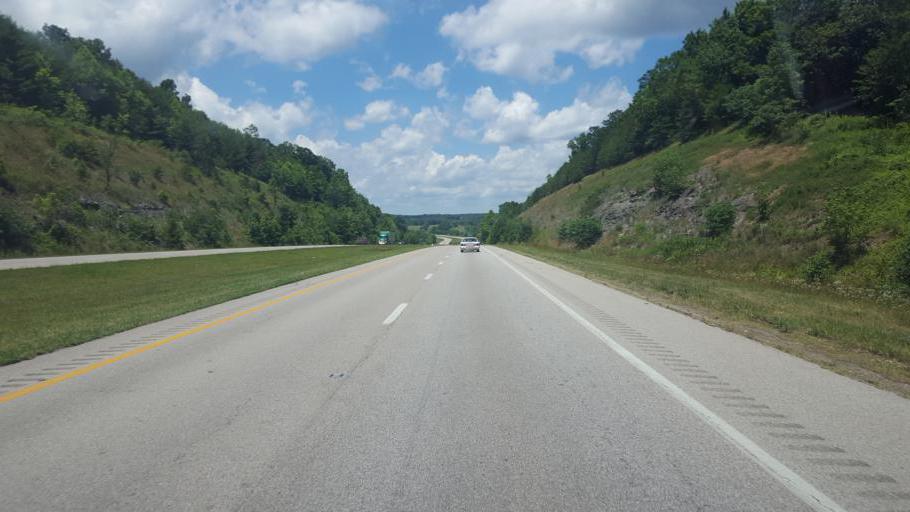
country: US
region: Ohio
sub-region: Gallia County
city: Gallipolis
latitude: 38.8883
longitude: -82.3500
